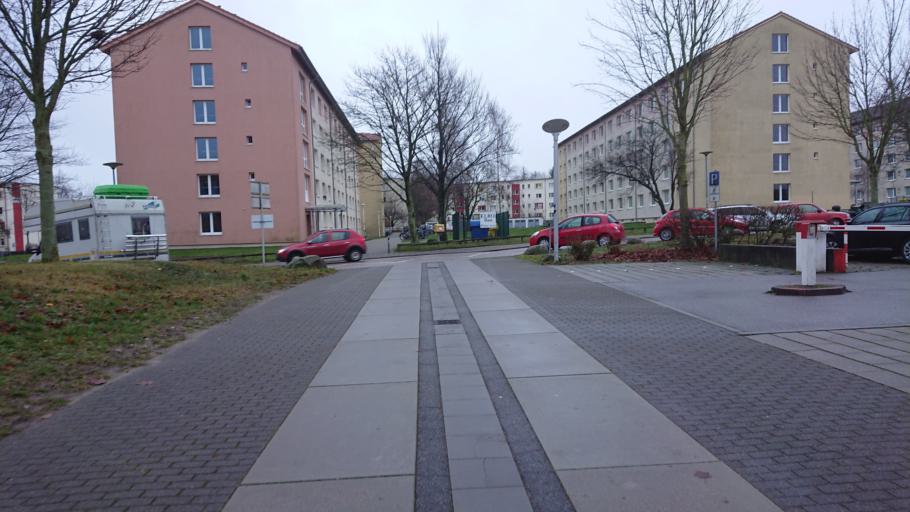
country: DE
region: Mecklenburg-Vorpommern
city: Rostock
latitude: 54.0764
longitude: 12.1128
